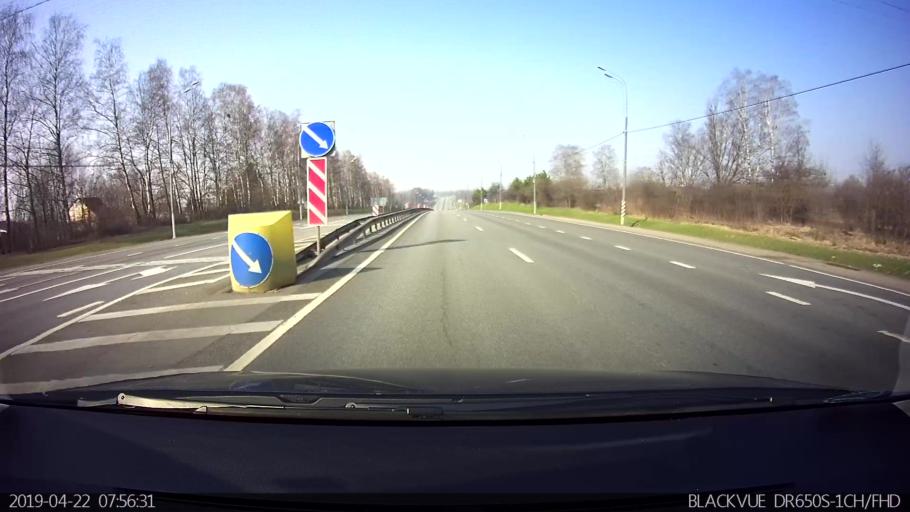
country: RU
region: Smolensk
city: Safonovo
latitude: 55.1395
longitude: 33.2346
